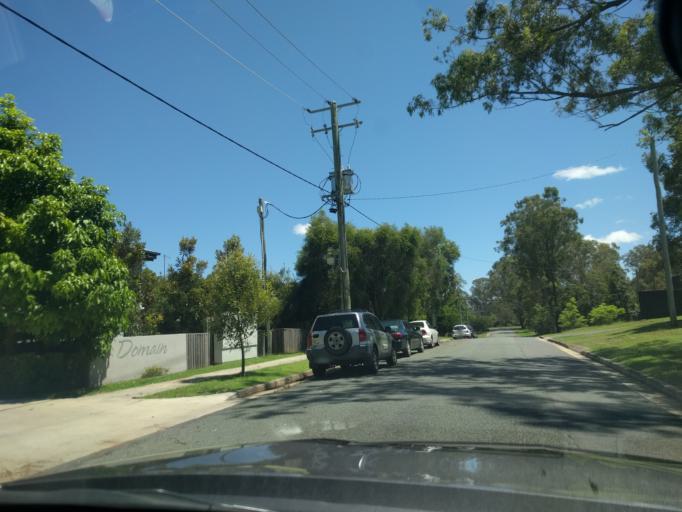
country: AU
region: Queensland
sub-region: Logan
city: Cedar Vale
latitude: -27.9868
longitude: 153.0073
